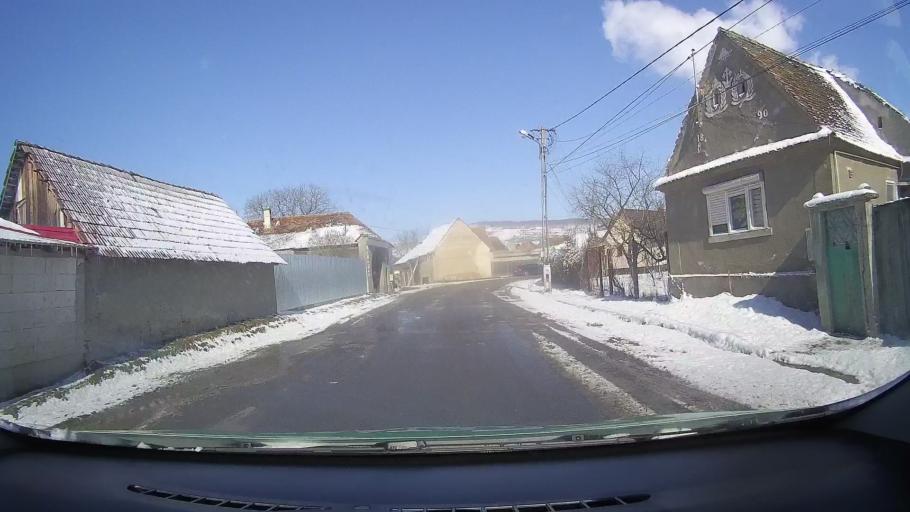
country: RO
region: Sibiu
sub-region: Comuna Avrig
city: Avrig
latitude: 45.7560
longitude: 24.3913
